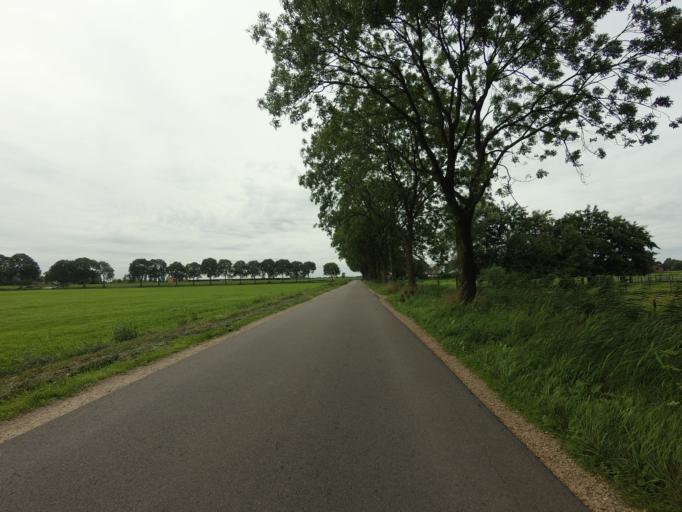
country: NL
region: Utrecht
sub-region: Gemeente De Ronde Venen
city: Mijdrecht
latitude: 52.2437
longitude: 4.8750
